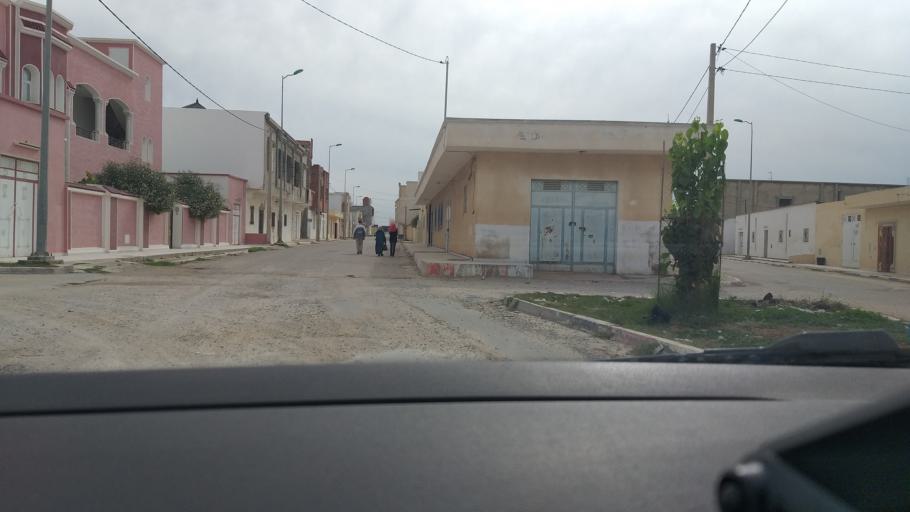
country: TN
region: Al Mahdiyah
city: El Jem
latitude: 35.2860
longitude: 10.7104
